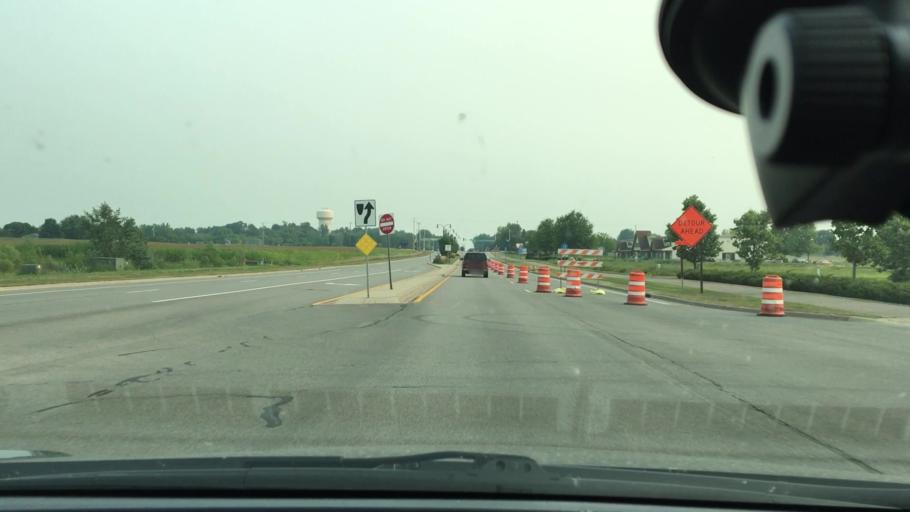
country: US
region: Minnesota
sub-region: Wright County
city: Albertville
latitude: 45.2287
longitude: -93.6645
